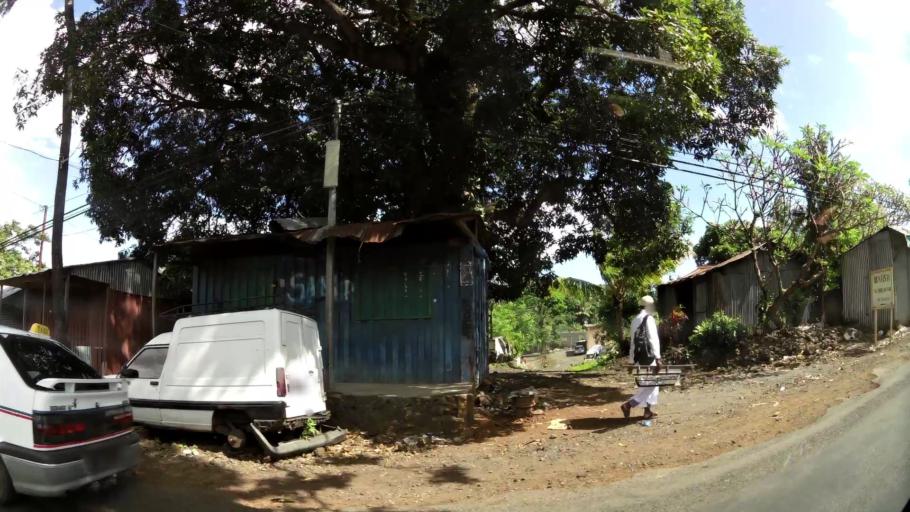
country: KM
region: Grande Comore
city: Mavingouni
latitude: -11.7355
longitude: 43.2498
